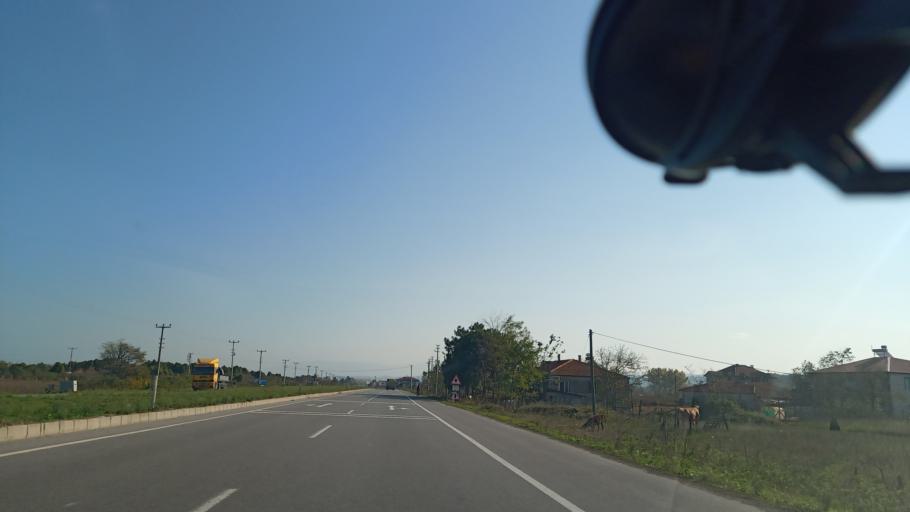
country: TR
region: Sakarya
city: Karasu
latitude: 41.0832
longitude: 30.7607
